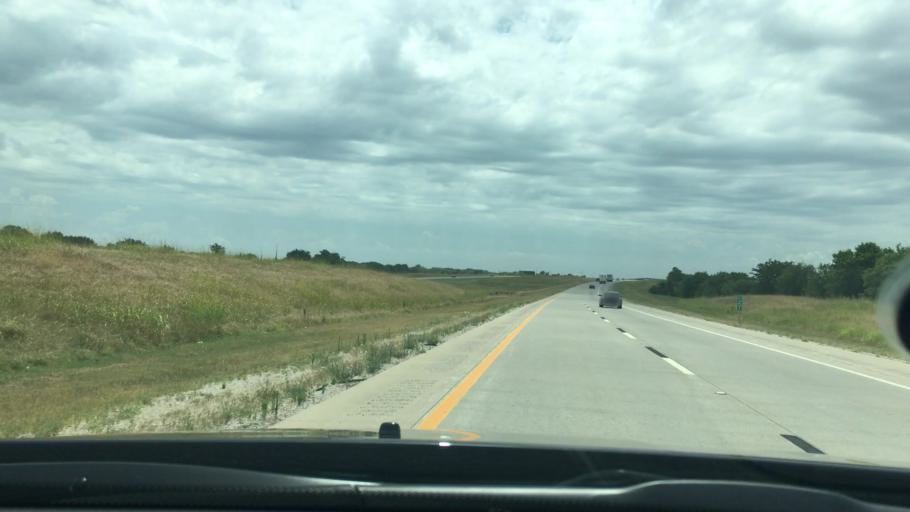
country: US
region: Oklahoma
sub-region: Carter County
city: Ardmore
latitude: 34.1087
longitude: -97.1524
